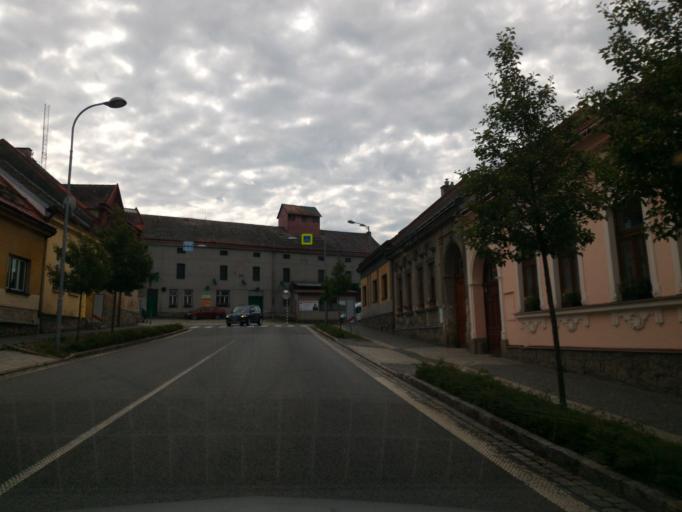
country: CZ
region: Vysocina
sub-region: Okres Jihlava
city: Telc
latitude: 49.1850
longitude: 15.4642
